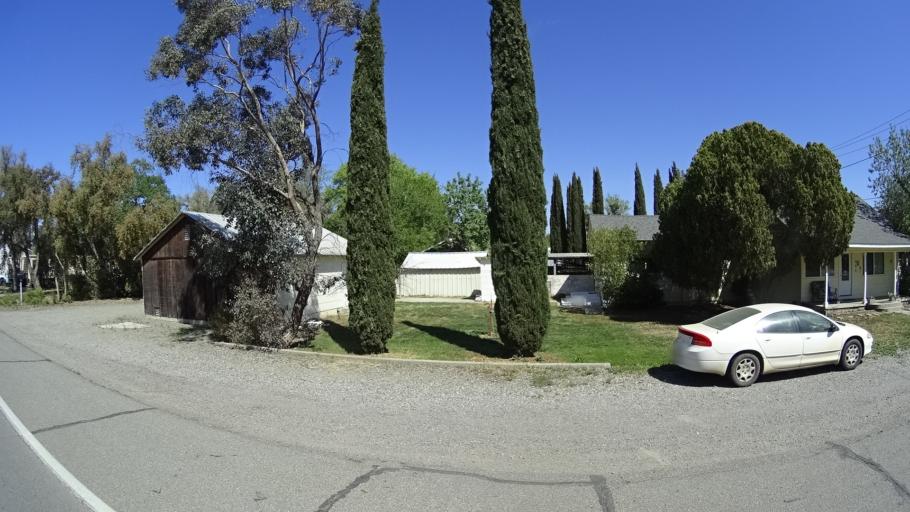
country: US
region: California
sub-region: Glenn County
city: Willows
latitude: 39.5242
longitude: -122.1870
